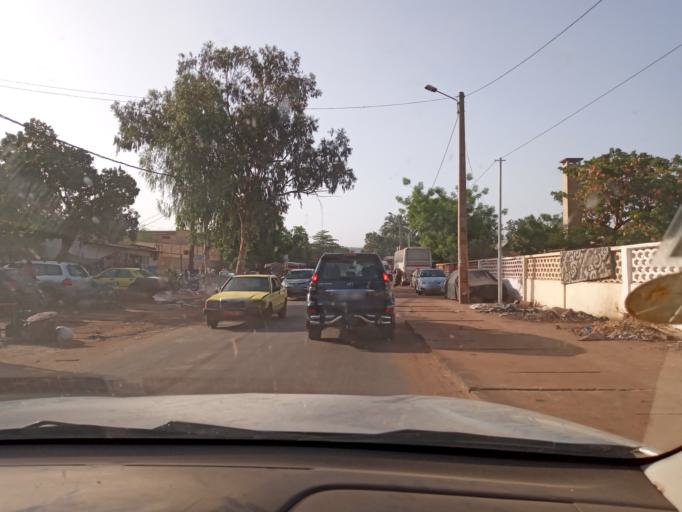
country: ML
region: Bamako
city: Bamako
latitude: 12.6582
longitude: -7.9714
